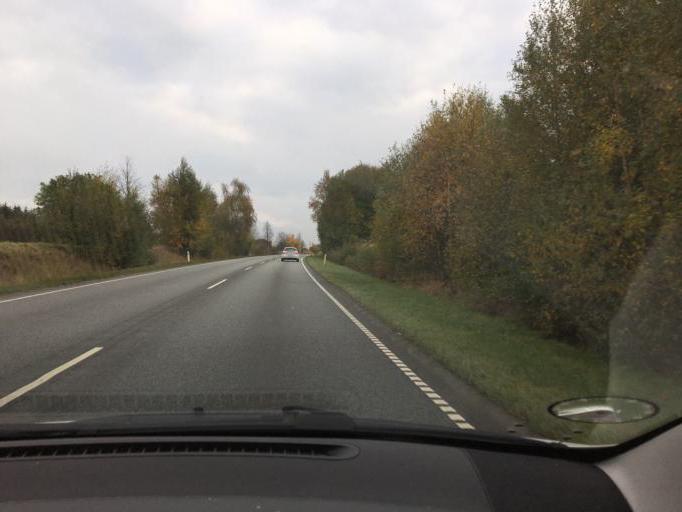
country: DK
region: South Denmark
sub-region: Fredericia Kommune
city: Fredericia
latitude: 55.6179
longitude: 9.7467
